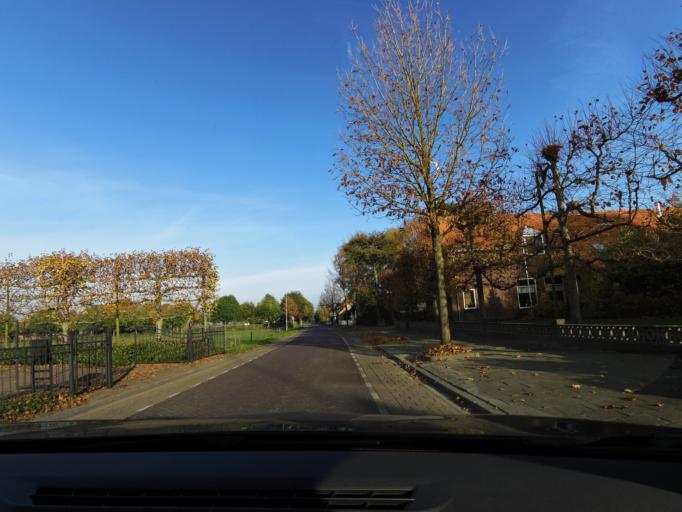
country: NL
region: North Brabant
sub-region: Gemeente Made en Drimmelen
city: Made
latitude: 51.6867
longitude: 4.8002
